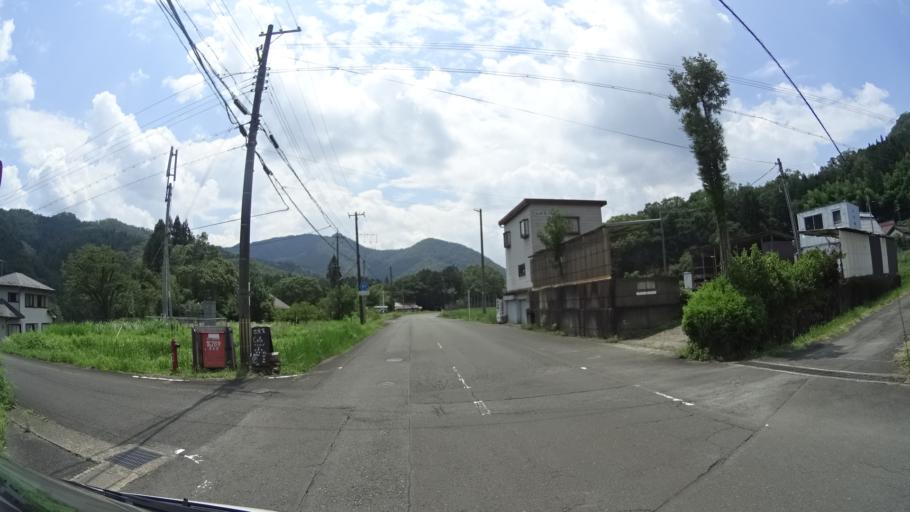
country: JP
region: Kyoto
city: Ayabe
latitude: 35.1798
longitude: 135.2793
